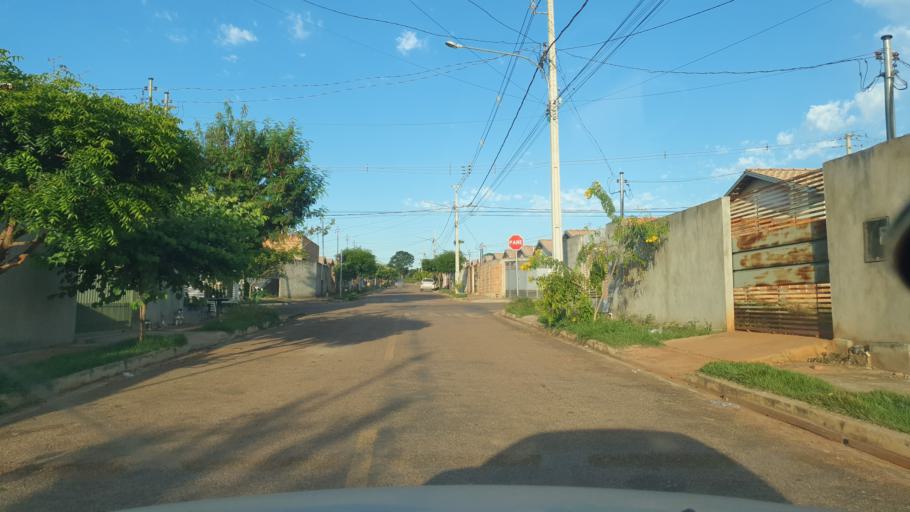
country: BR
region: Mato Grosso
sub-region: Pontes E Lacerda
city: Pontes e Lacerda
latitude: -15.2285
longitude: -59.3121
